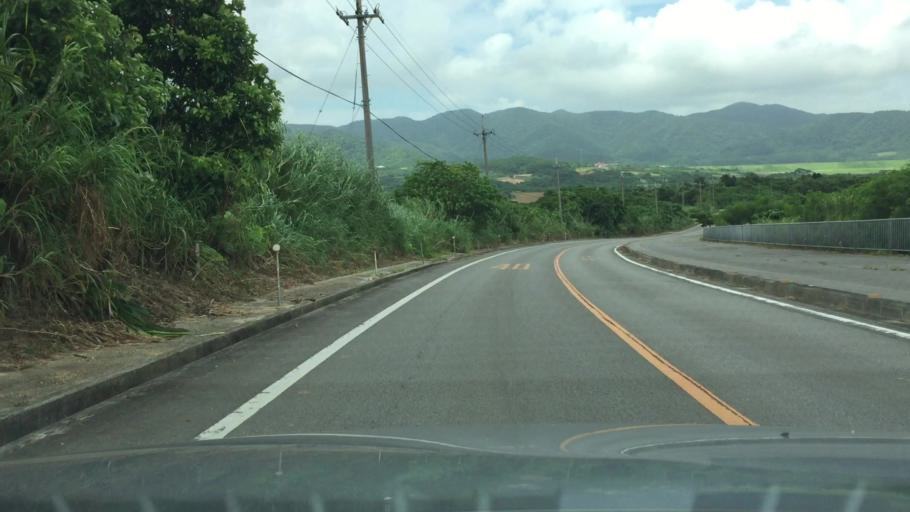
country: JP
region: Okinawa
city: Ishigaki
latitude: 24.4022
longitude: 124.2126
